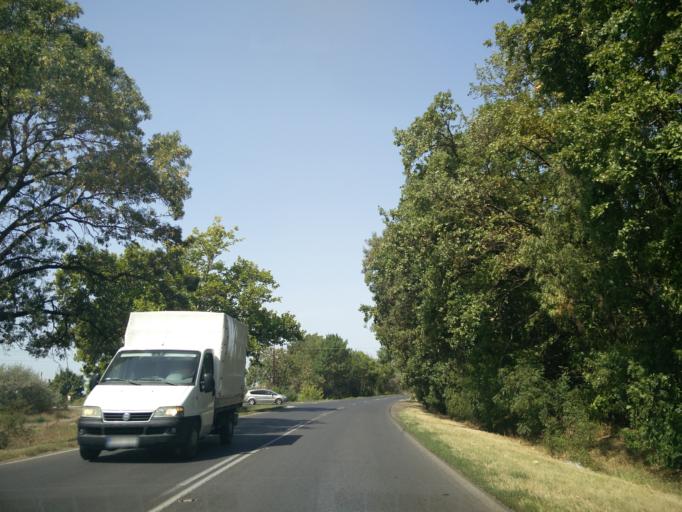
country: HU
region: Csongrad
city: Szatymaz
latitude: 46.3005
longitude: 20.0735
